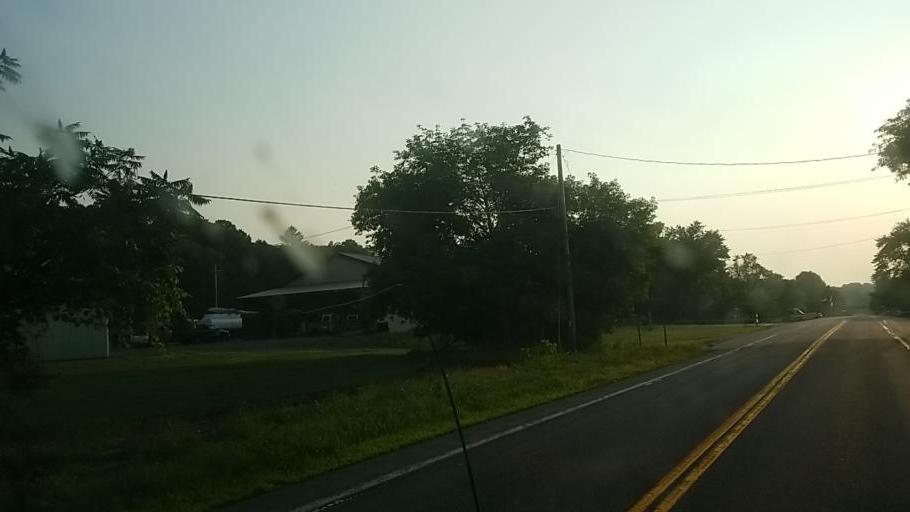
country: US
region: New York
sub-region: Montgomery County
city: Canajoharie
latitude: 42.8913
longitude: -74.5123
